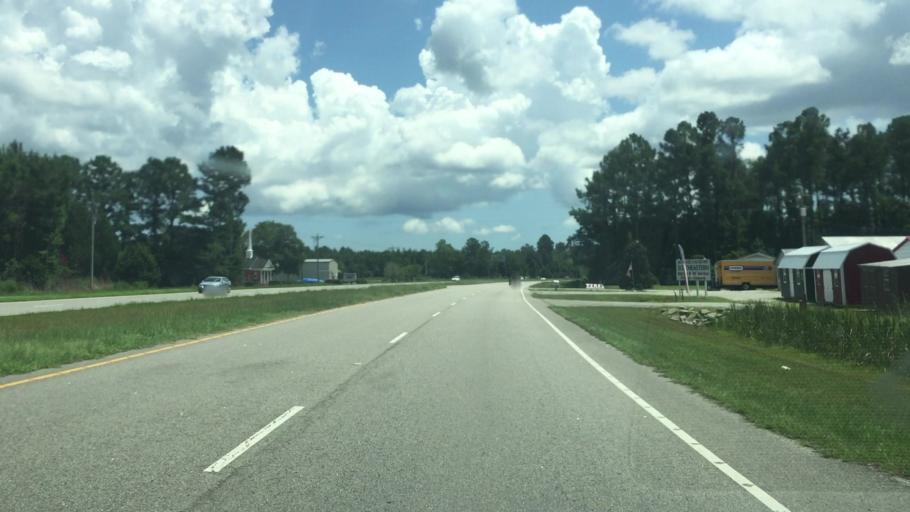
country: US
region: South Carolina
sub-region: Horry County
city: Loris
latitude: 34.0004
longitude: -78.7546
